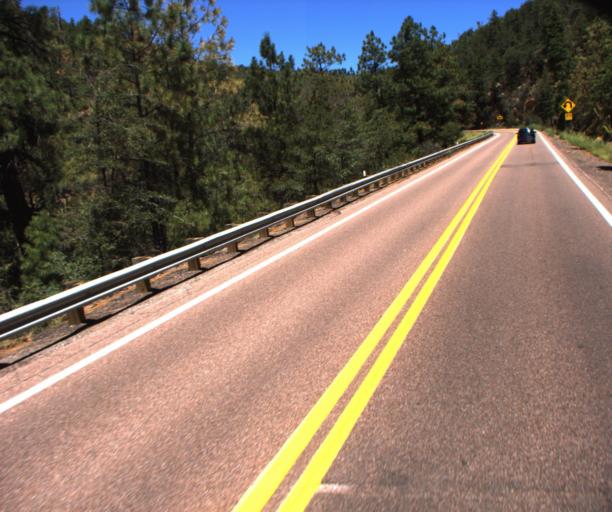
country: US
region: Arizona
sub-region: Gila County
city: Pine
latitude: 34.4199
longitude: -111.5010
